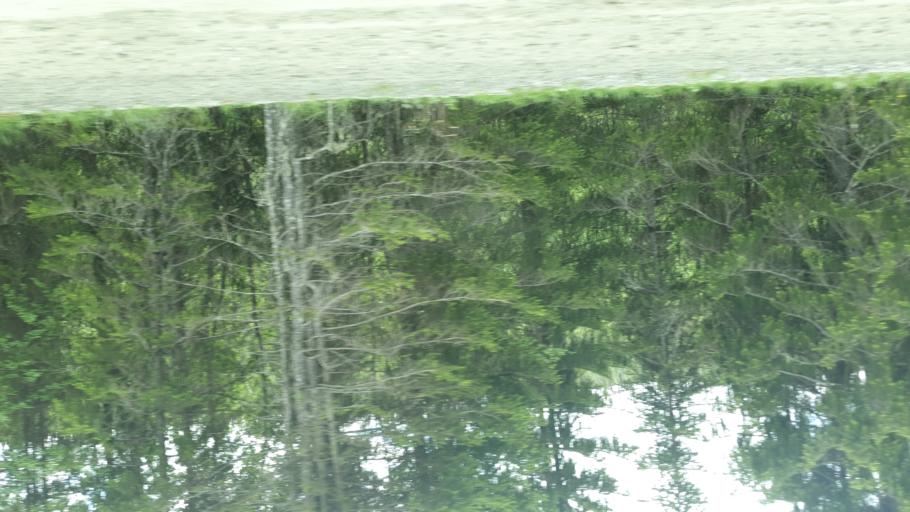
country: NO
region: Sor-Trondelag
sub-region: Trondheim
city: Trondheim
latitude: 63.6804
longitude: 10.3536
